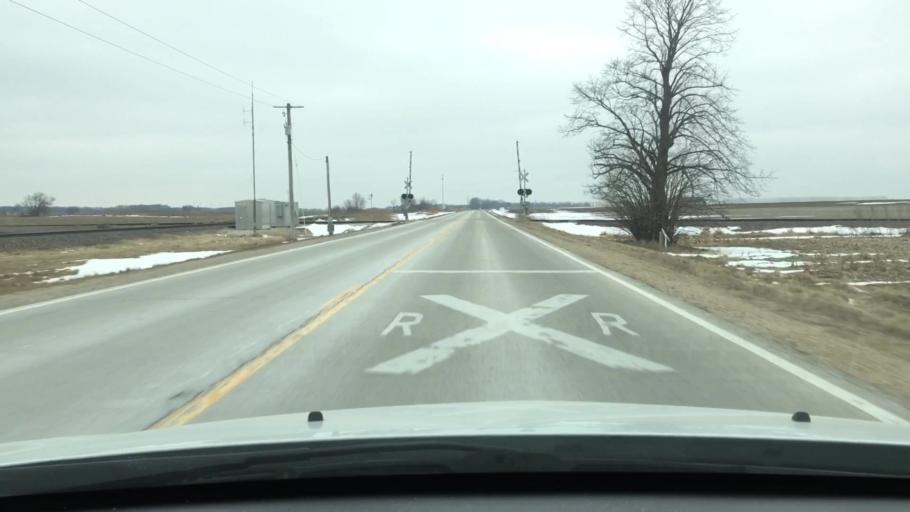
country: US
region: Illinois
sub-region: DeKalb County
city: Waterman
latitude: 41.7688
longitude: -88.8281
